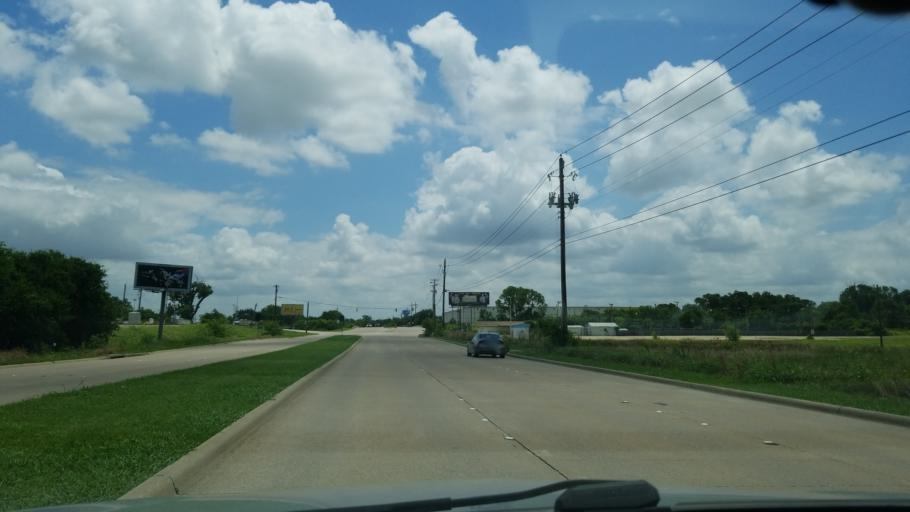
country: US
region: Texas
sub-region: Dallas County
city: Carrollton
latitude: 32.9516
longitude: -96.9421
